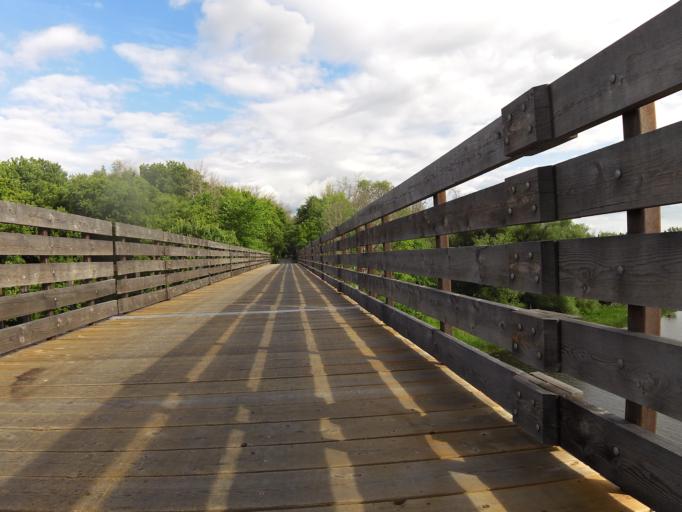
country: CA
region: Ontario
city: Arnprior
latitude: 45.3261
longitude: -76.2892
